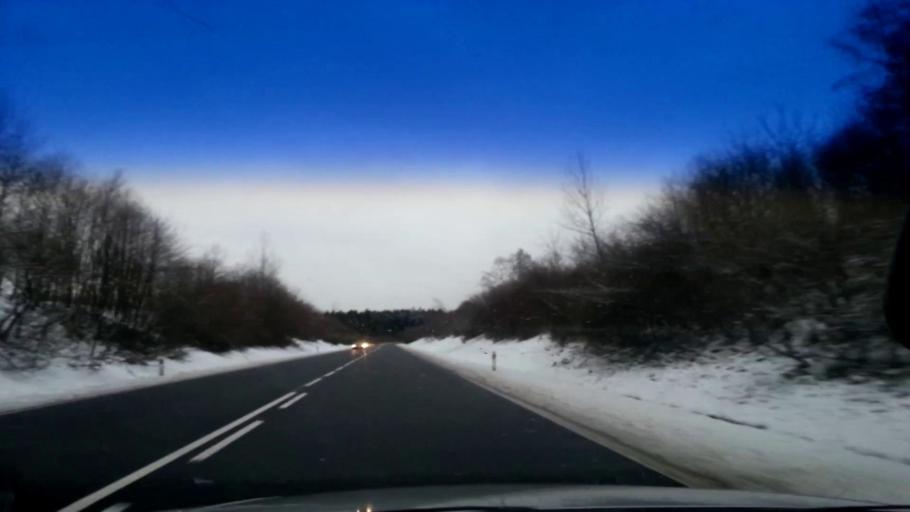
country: CZ
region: Karlovarsky
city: As
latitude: 50.2074
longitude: 12.1883
